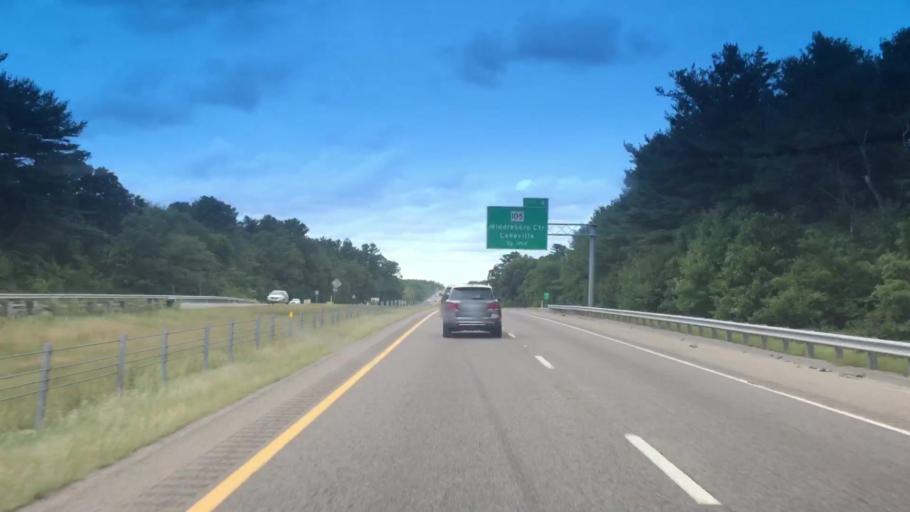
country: US
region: Massachusetts
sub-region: Plymouth County
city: Middleborough Center
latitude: 41.8761
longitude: -70.9054
